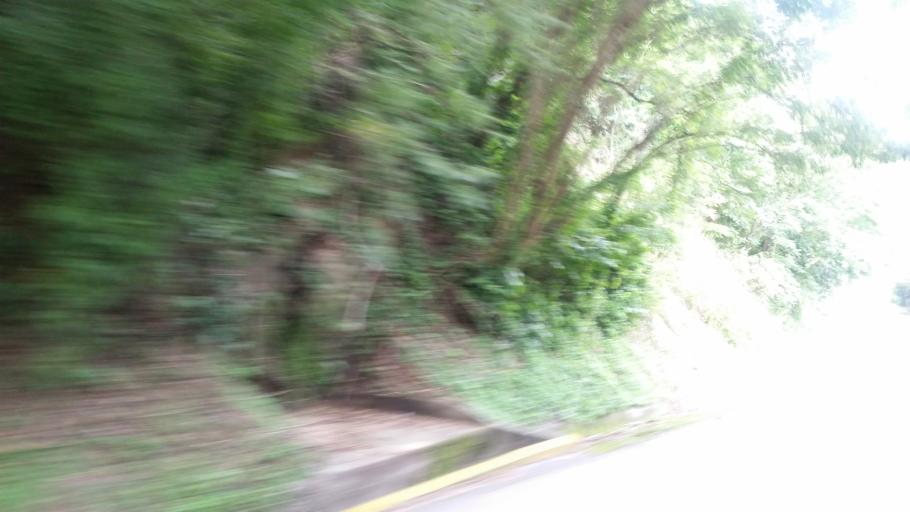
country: CO
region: Magdalena
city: Santa Marta
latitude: 11.2770
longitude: -74.0416
